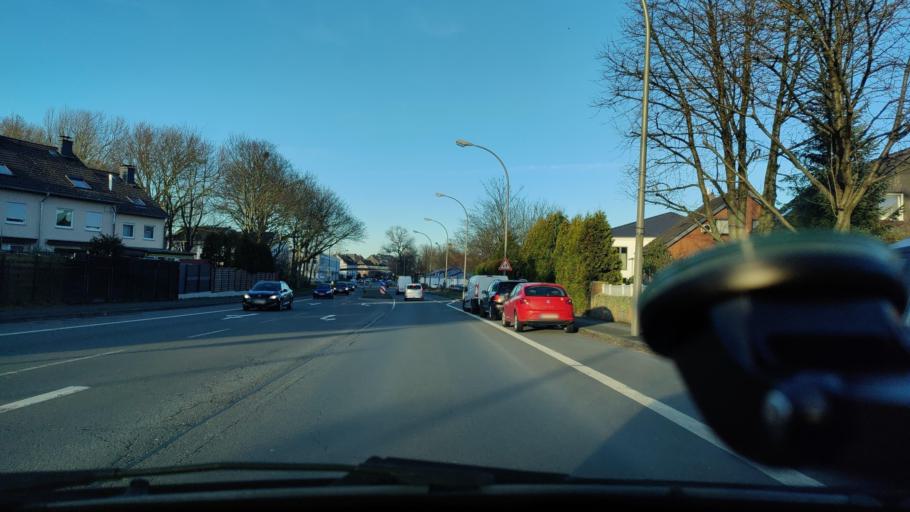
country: DE
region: North Rhine-Westphalia
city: Castrop-Rauxel
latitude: 51.5641
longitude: 7.3686
